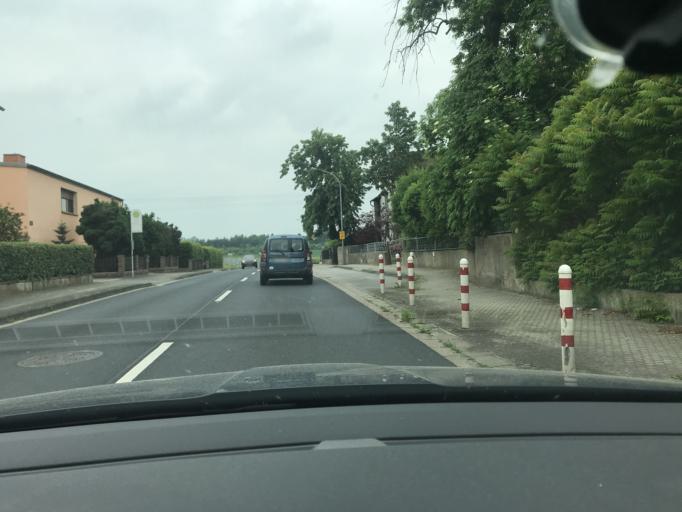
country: DE
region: Saxony
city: Priestewitz
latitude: 51.2497
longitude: 13.5056
